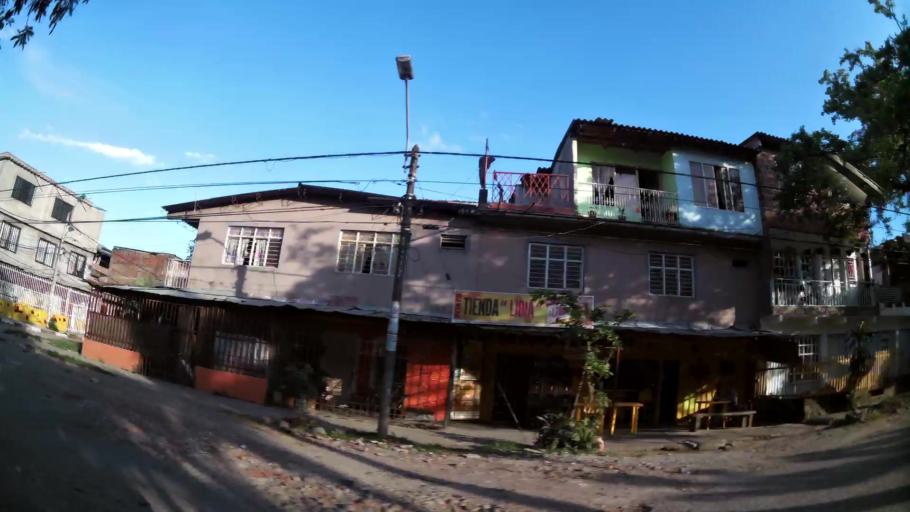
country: CO
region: Valle del Cauca
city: Cali
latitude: 3.4110
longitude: -76.5038
